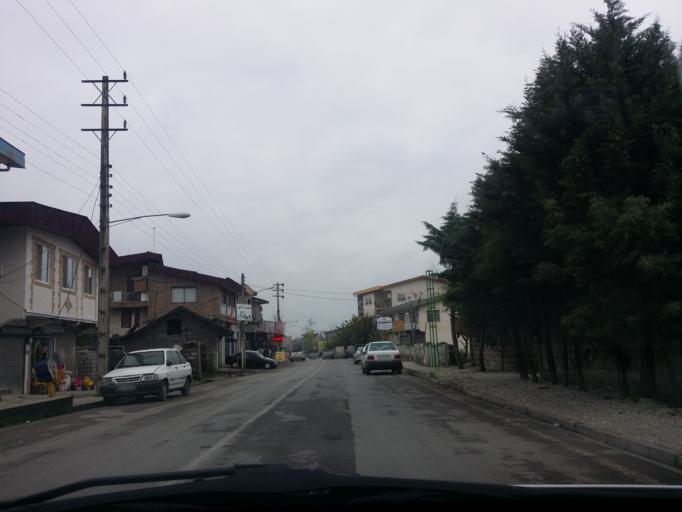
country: IR
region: Mazandaran
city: Chalus
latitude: 36.6637
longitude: 51.3930
